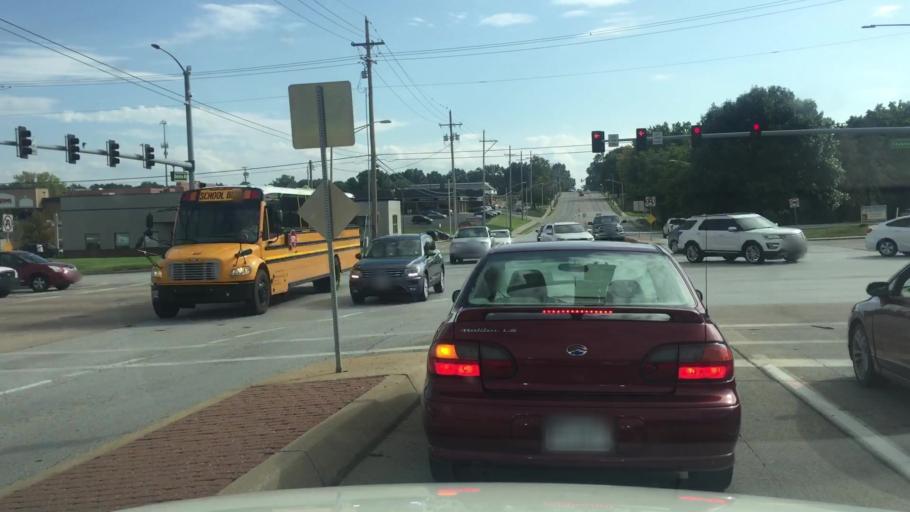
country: US
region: Kansas
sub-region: Johnson County
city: Shawnee
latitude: 39.0150
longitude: -94.7238
